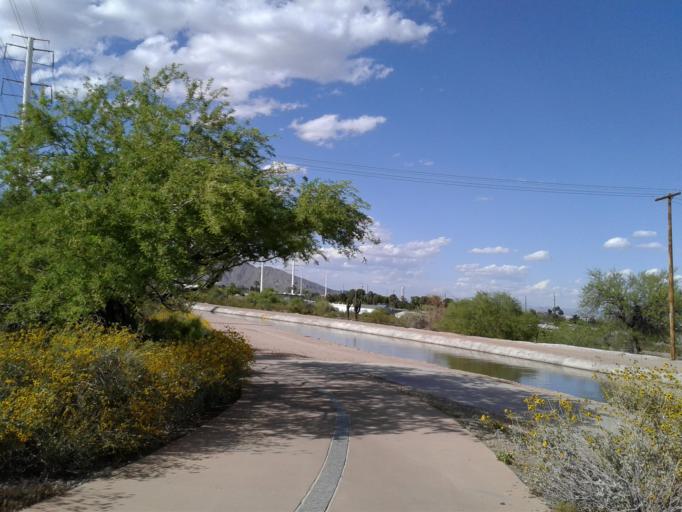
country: US
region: Arizona
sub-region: Maricopa County
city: Tempe Junction
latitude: 33.4510
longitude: -111.9404
